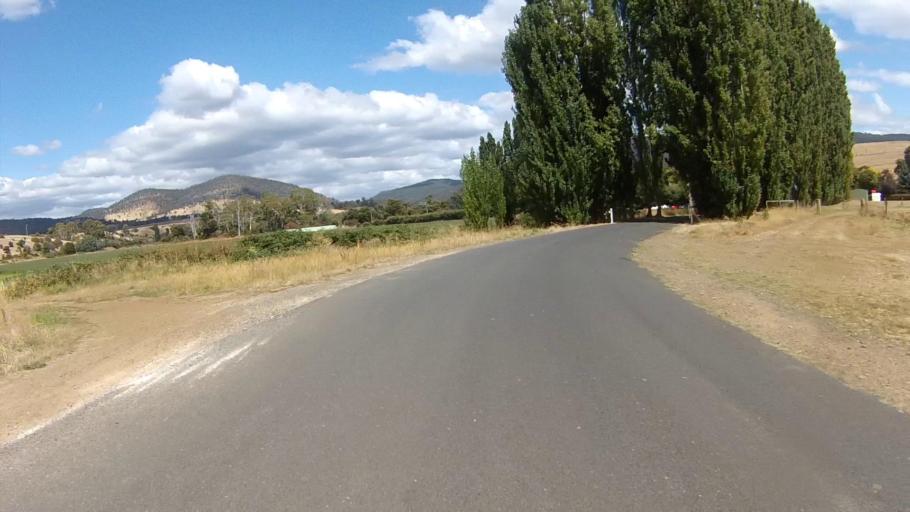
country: AU
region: Tasmania
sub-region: Derwent Valley
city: New Norfolk
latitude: -42.7526
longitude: 146.9718
